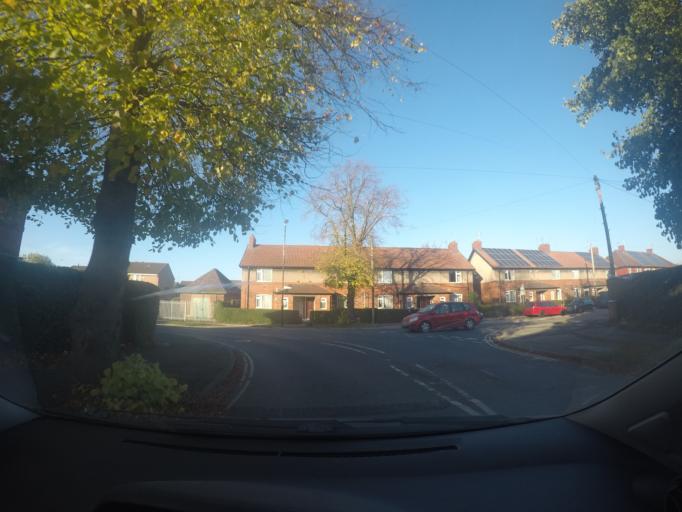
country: GB
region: England
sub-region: City of York
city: York
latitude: 53.9729
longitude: -1.0709
